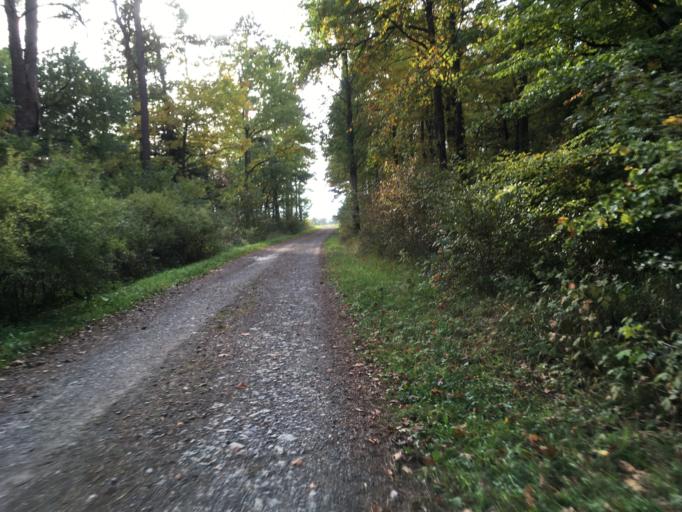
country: DE
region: Baden-Wuerttemberg
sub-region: Karlsruhe Region
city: Hopfingen
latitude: 49.5205
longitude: 9.4201
